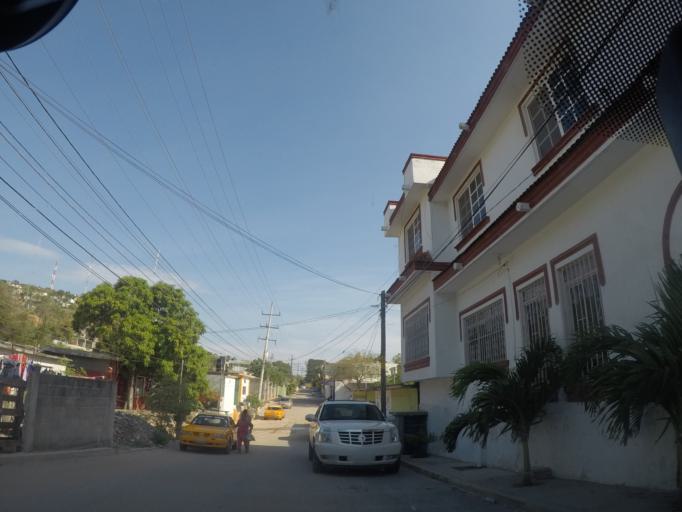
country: MX
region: Oaxaca
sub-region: Salina Cruz
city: Salina Cruz
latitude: 16.1984
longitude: -95.2027
